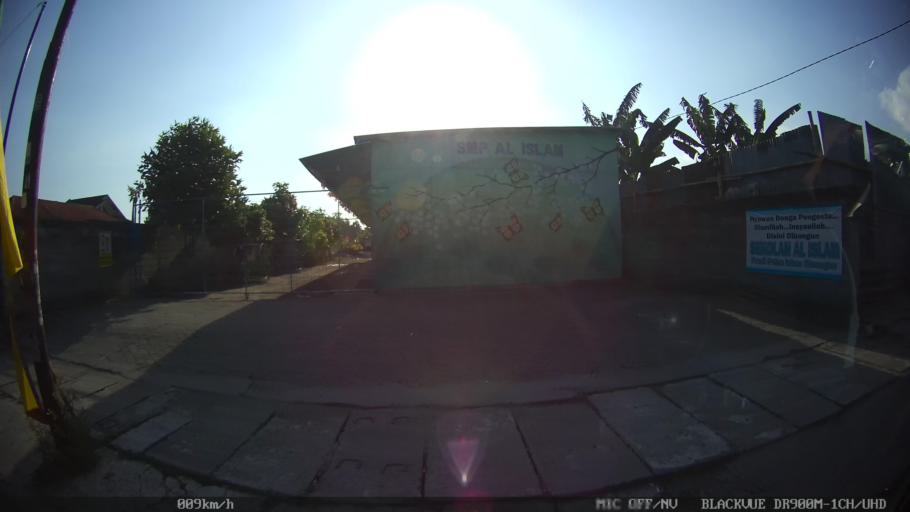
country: ID
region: Daerah Istimewa Yogyakarta
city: Yogyakarta
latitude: -7.8240
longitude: 110.3881
